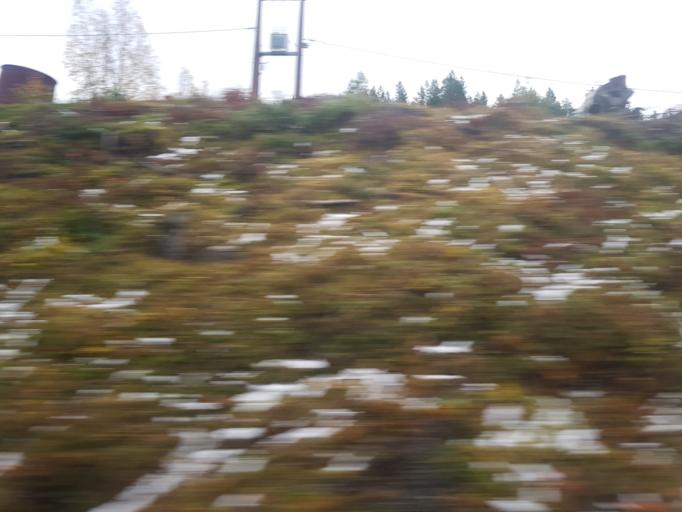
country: NO
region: Sor-Trondelag
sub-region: Rennebu
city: Berkak
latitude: 62.6887
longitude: 9.9304
